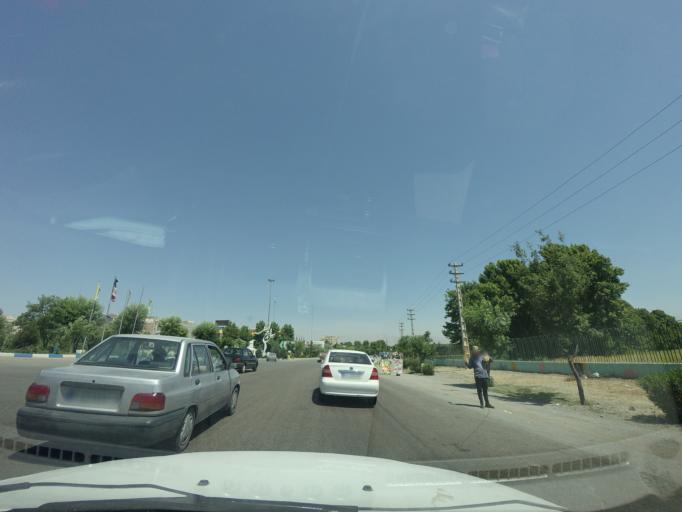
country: IR
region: Tehran
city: Eslamshahr
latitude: 35.6394
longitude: 51.2177
